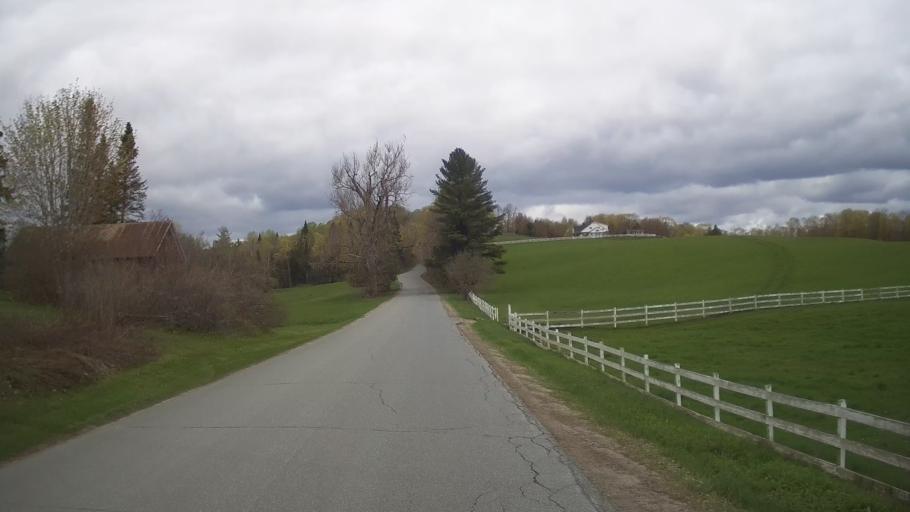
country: US
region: Vermont
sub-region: Caledonia County
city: Lyndonville
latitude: 44.5923
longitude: -71.9585
